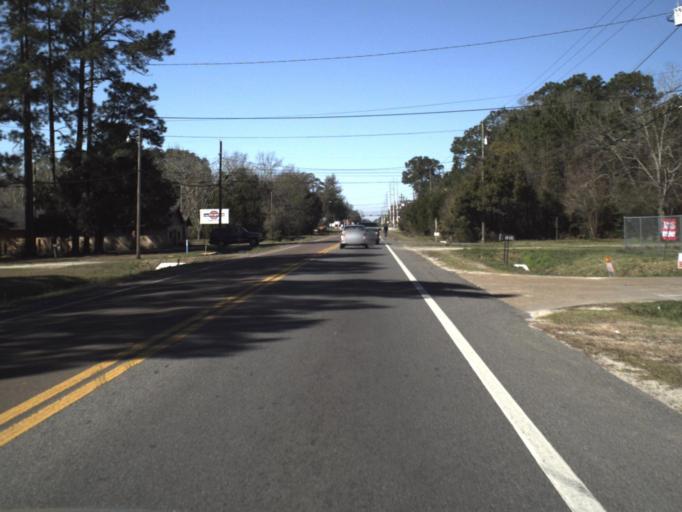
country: US
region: Florida
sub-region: Bay County
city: Springfield
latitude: 30.1530
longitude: -85.5944
